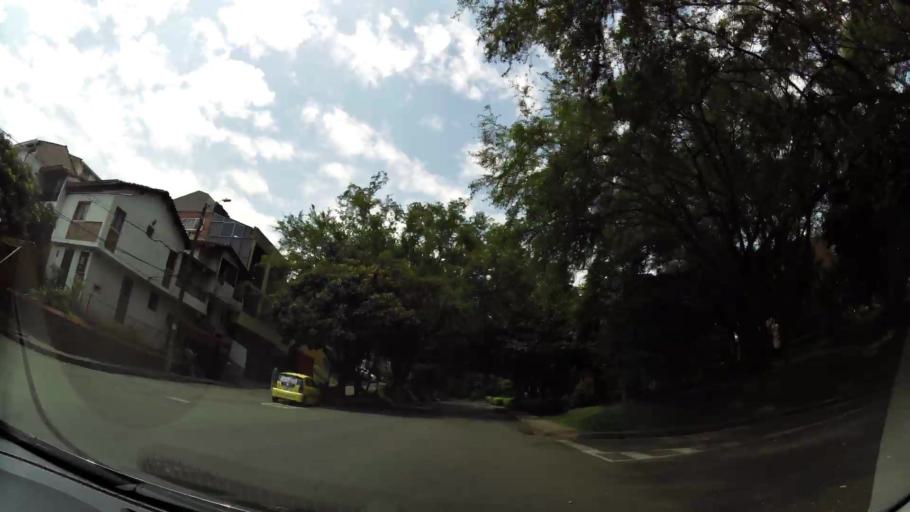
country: CO
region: Antioquia
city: Medellin
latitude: 6.2500
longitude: -75.6150
